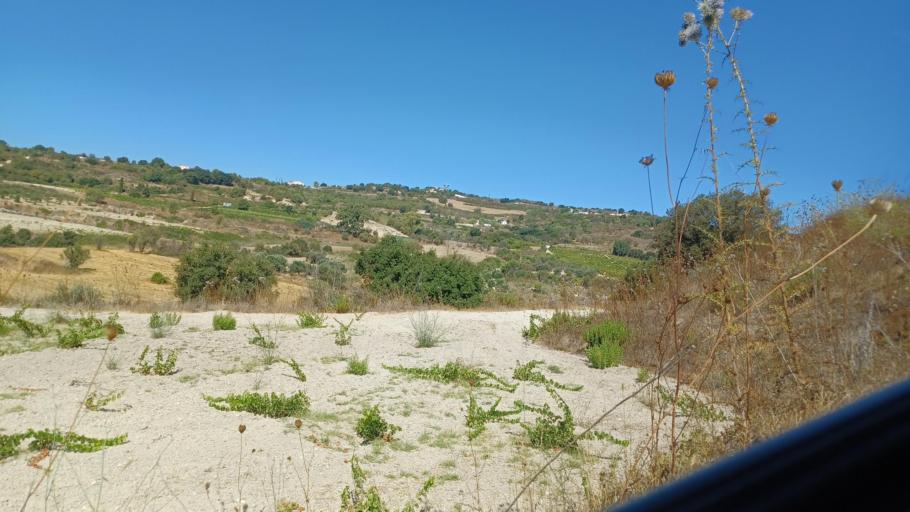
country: CY
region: Pafos
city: Mesogi
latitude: 34.8731
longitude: 32.5156
